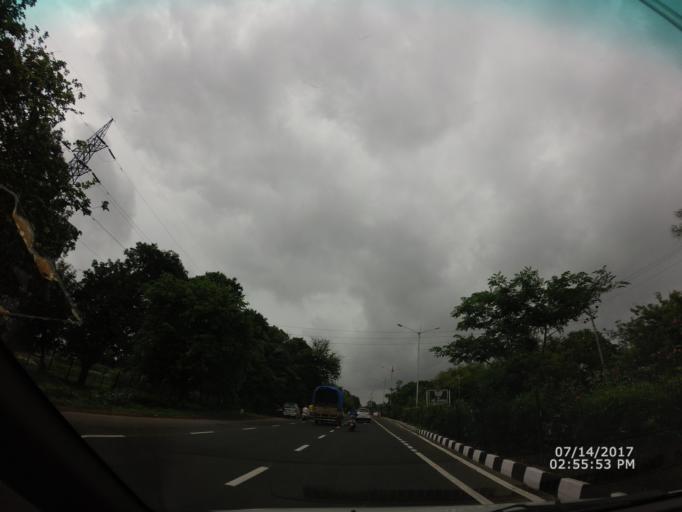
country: IN
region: Gujarat
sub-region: Gandhinagar
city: Adalaj
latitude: 23.1464
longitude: 72.6342
